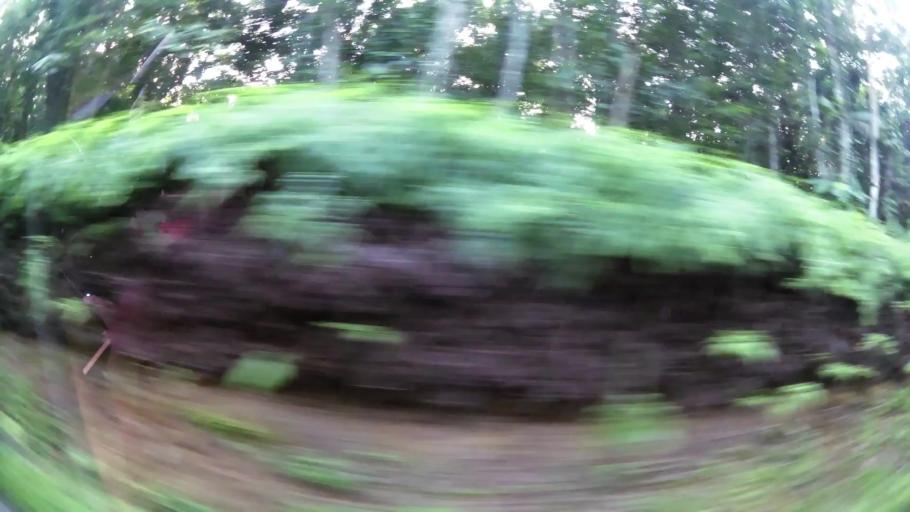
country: GP
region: Guadeloupe
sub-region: Guadeloupe
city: Petit-Bourg
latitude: 16.1818
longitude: -61.6812
